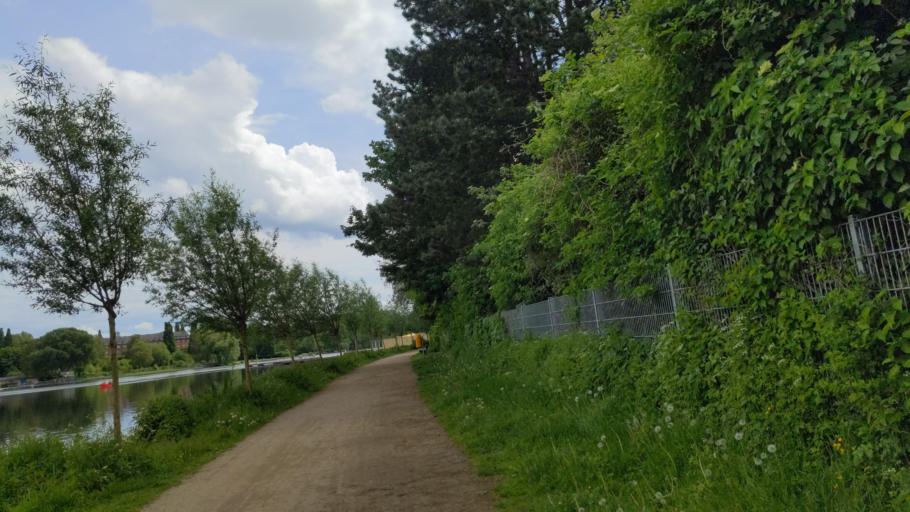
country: DE
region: Schleswig-Holstein
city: Luebeck
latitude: 53.8711
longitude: 10.7030
